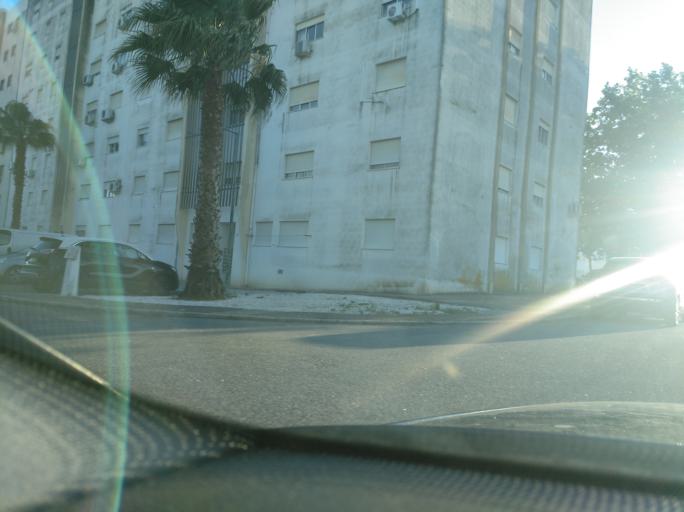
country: PT
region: Portalegre
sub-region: Elvas
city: Elvas
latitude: 38.8773
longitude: -7.1837
